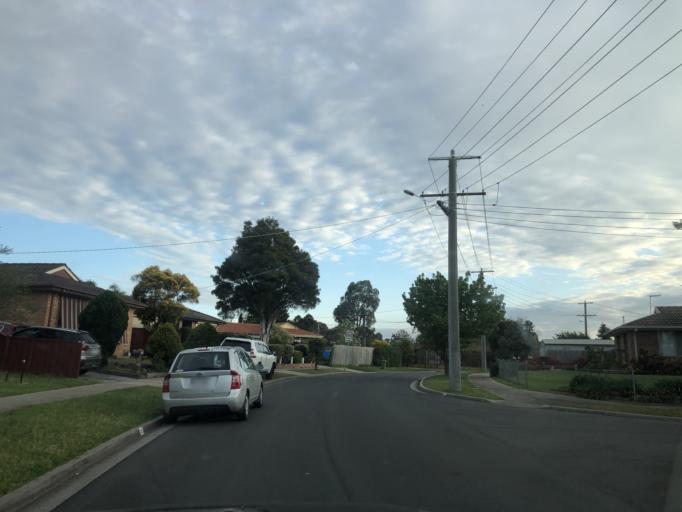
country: AU
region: Victoria
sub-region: Casey
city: Hampton Park
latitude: -38.0312
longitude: 145.2555
